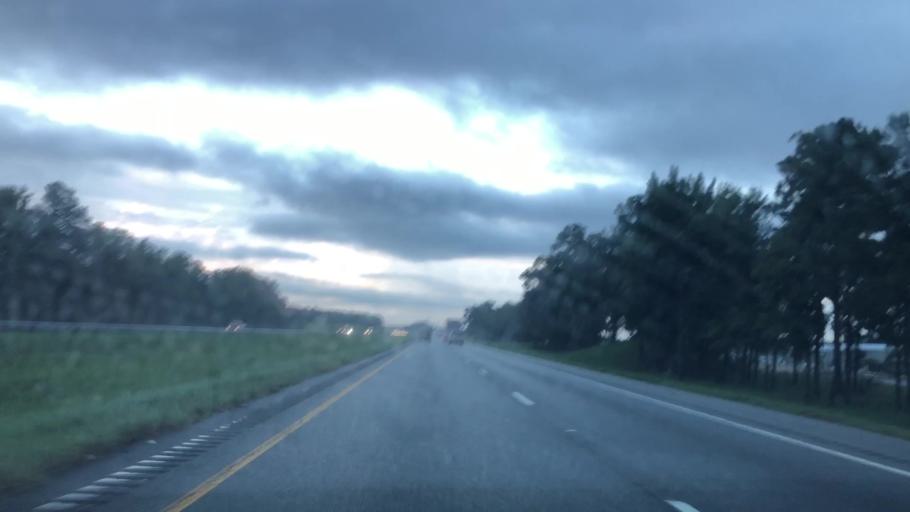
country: US
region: Alabama
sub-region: Shelby County
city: Alabaster
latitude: 33.1791
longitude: -86.7805
